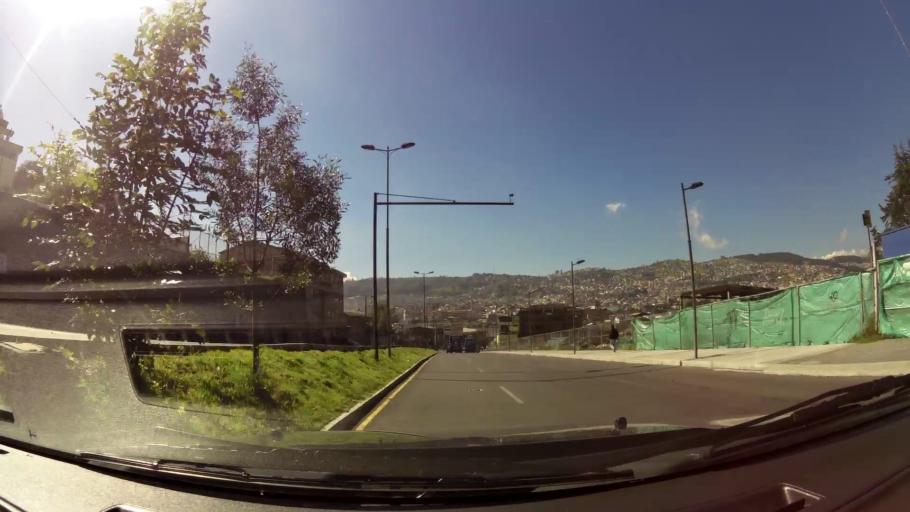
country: EC
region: Pichincha
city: Quito
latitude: -0.2385
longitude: -78.5245
